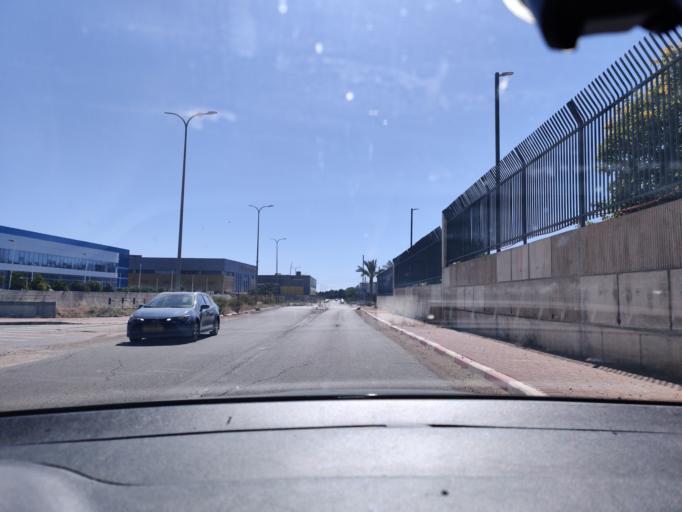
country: IL
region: Southern District
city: Qiryat Gat
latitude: 31.5912
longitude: 34.7883
